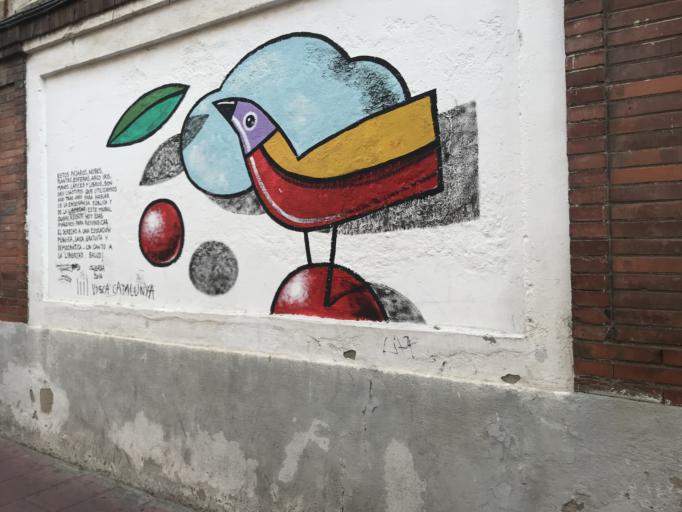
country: ES
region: Castille and Leon
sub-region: Provincia de Valladolid
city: Valladolid
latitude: 41.6528
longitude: -4.7189
